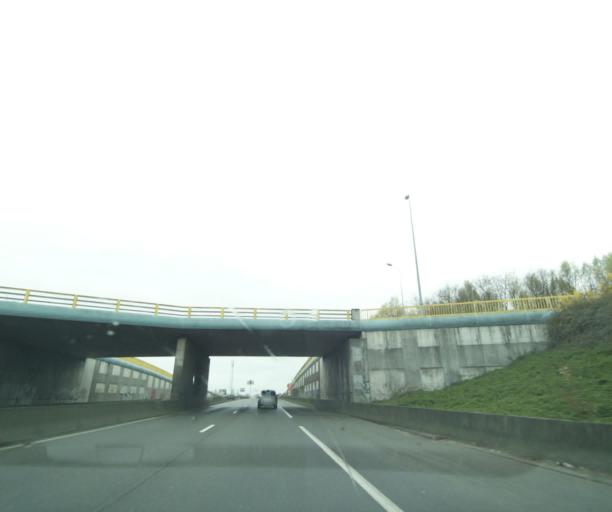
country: FR
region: Ile-de-France
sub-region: Departement de l'Essonne
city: Arpajon
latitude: 48.5983
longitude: 2.2450
